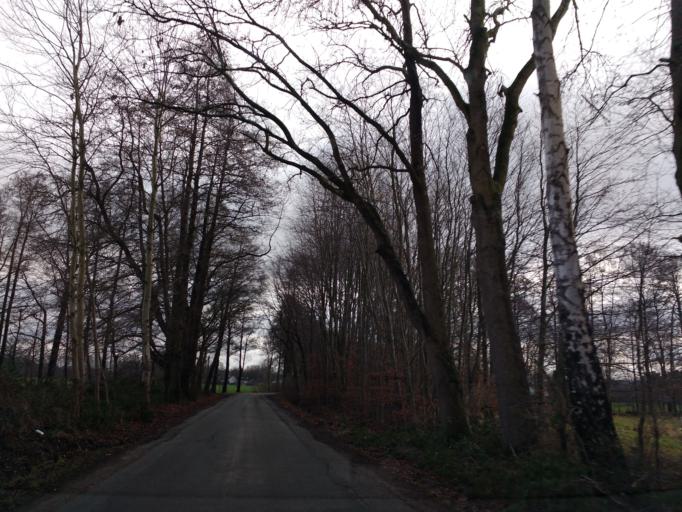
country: DE
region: North Rhine-Westphalia
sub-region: Regierungsbezirk Detmold
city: Hovelhof
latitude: 51.8249
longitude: 8.6902
